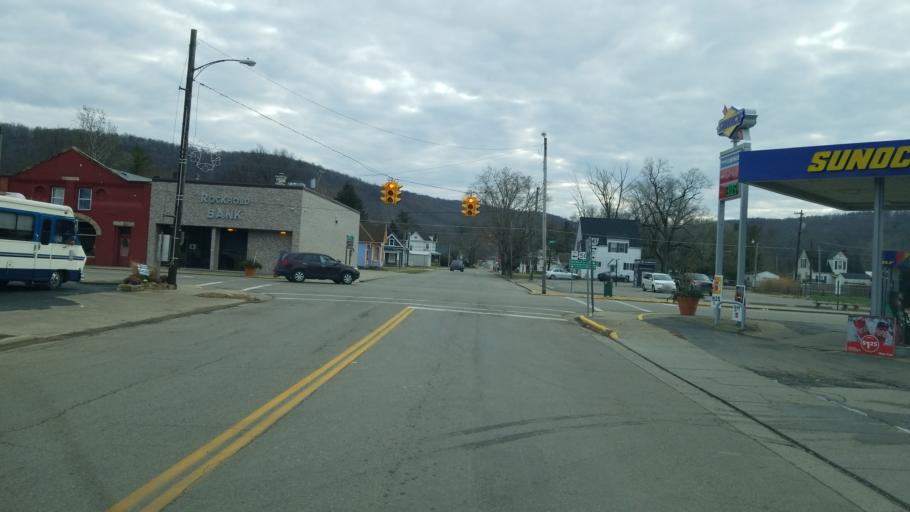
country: US
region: Ohio
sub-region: Highland County
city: Greenfield
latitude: 39.2283
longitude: -83.2704
